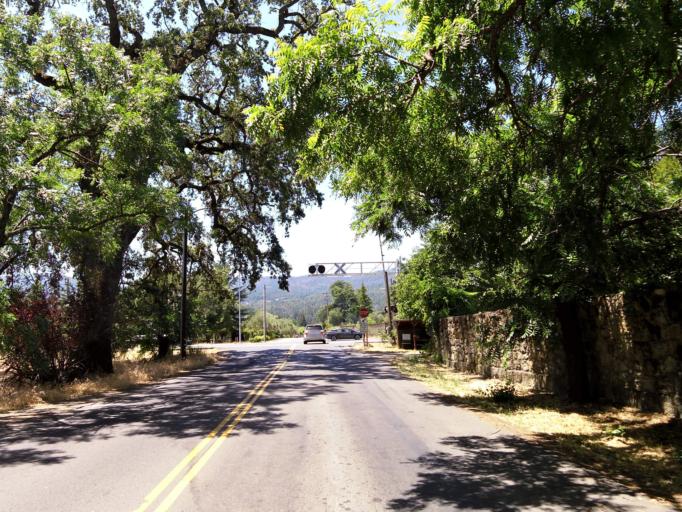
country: US
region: California
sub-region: Napa County
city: Saint Helena
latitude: 38.4830
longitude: -122.4421
